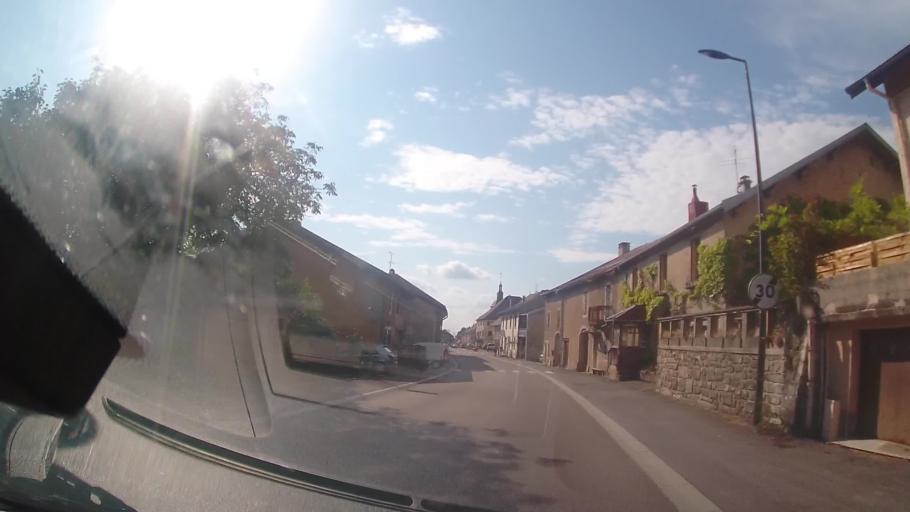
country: FR
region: Franche-Comte
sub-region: Departement du Jura
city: Clairvaux-les-Lacs
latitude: 46.6001
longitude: 5.8568
